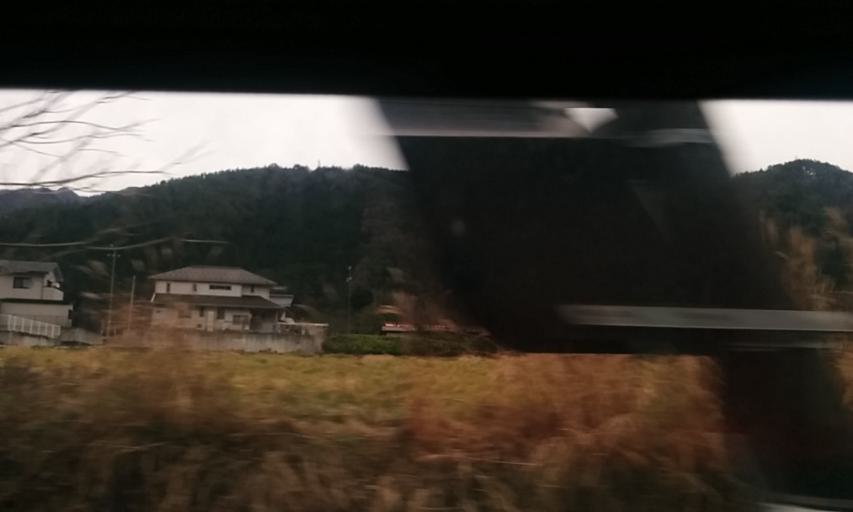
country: JP
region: Nagano
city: Ina
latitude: 35.8808
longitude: 137.7549
